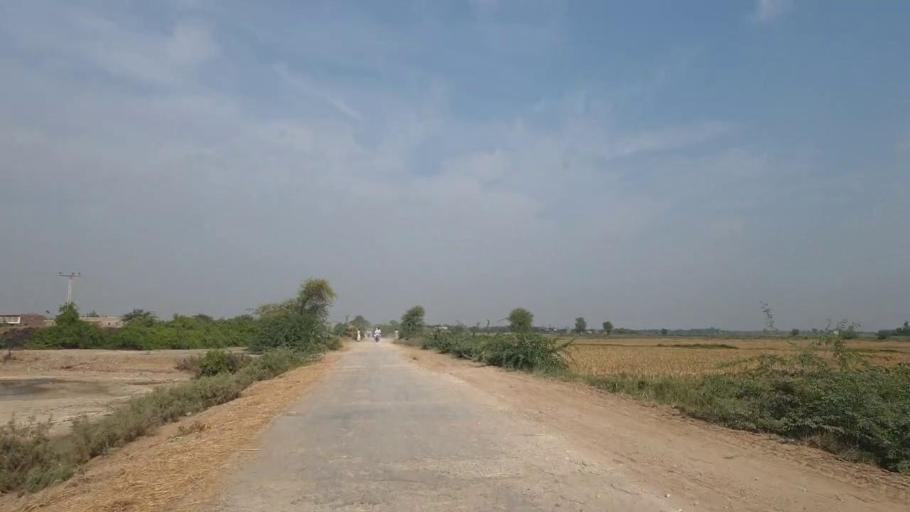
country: PK
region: Sindh
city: Tando Bago
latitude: 24.9081
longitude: 68.9965
